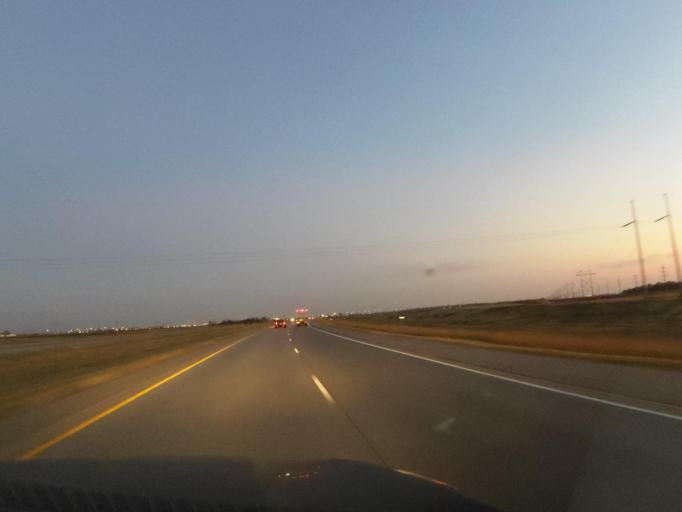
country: US
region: North Dakota
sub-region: Cass County
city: West Fargo
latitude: 46.9664
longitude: -96.8723
